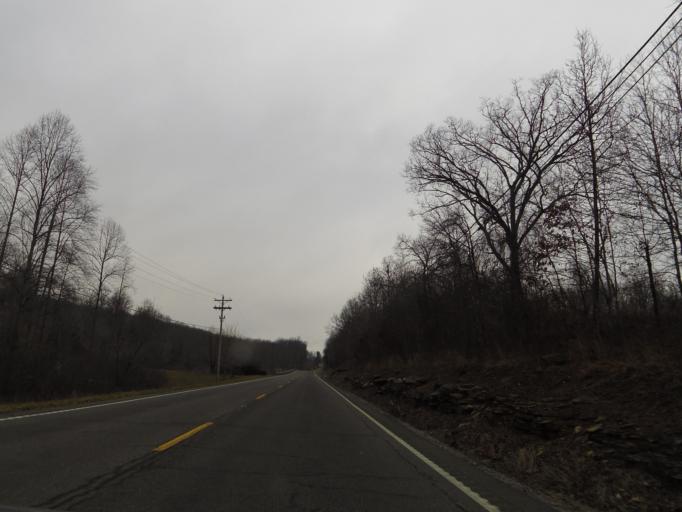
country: US
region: Tennessee
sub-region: Morgan County
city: Wartburg
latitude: 36.2058
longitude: -84.6608
